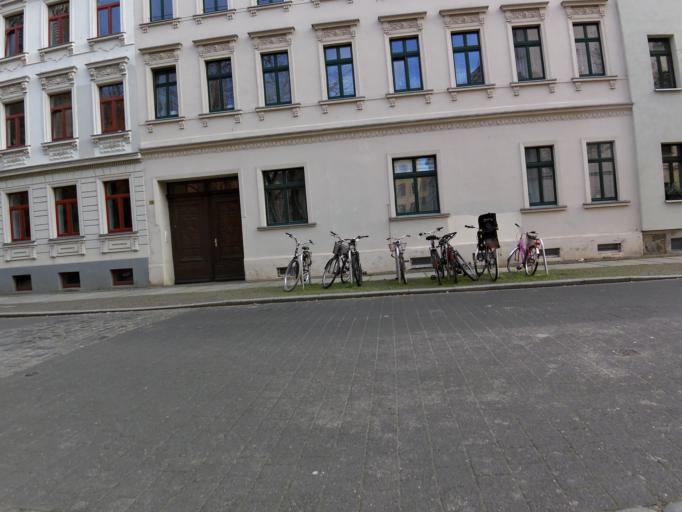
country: DE
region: Saxony
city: Leipzig
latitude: 51.3477
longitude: 12.4029
